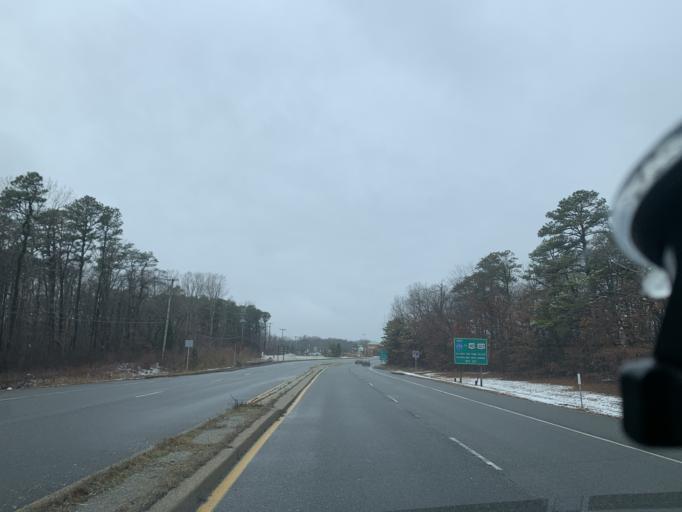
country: US
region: New Jersey
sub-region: Atlantic County
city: Pomona
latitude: 39.4498
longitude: -74.6347
